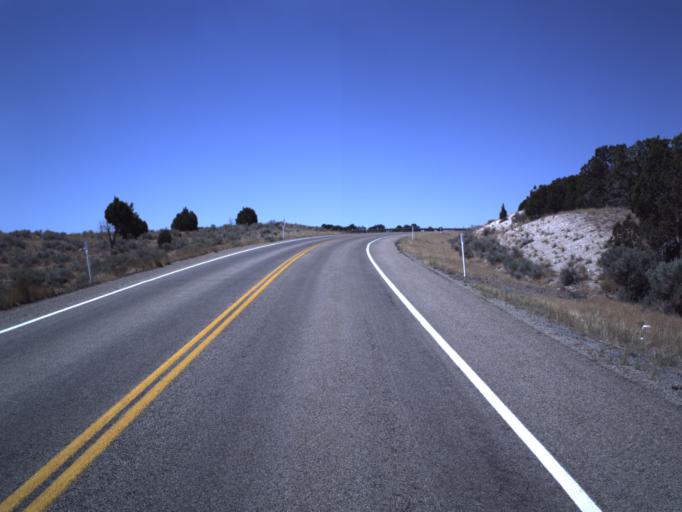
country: US
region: Utah
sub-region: Juab County
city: Nephi
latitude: 39.6655
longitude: -112.0441
